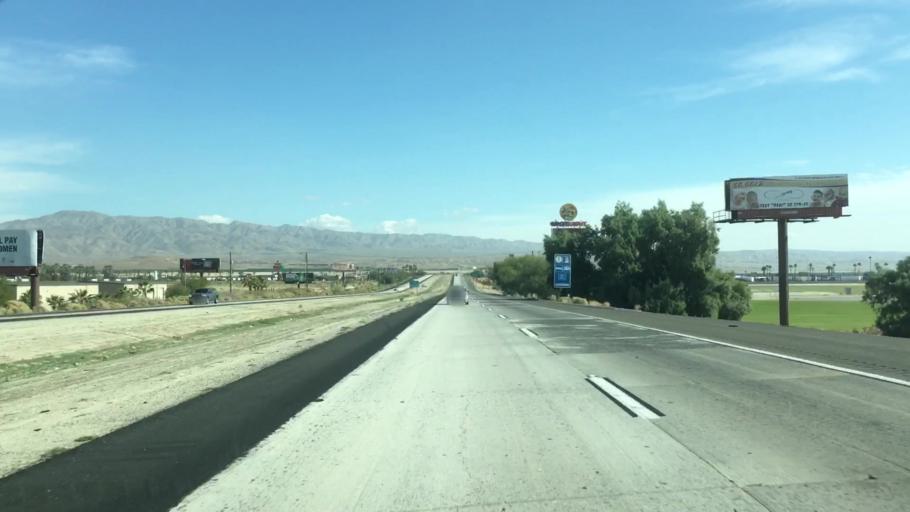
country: US
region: California
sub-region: Riverside County
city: Indio
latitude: 33.7150
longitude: -116.1844
